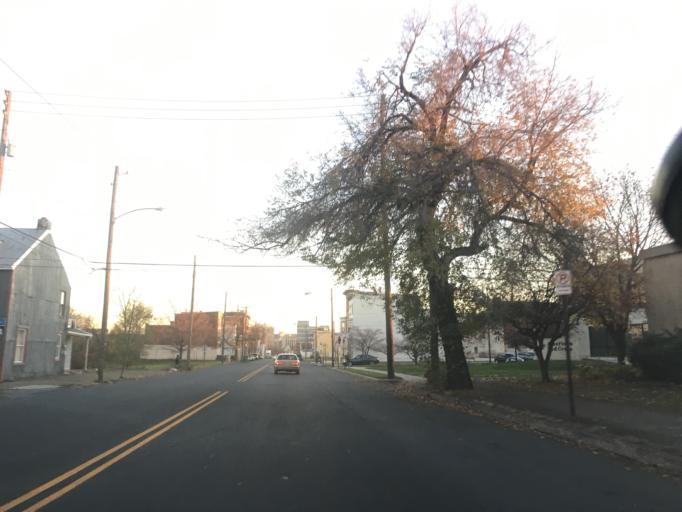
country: US
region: Pennsylvania
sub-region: Dauphin County
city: Harrisburg
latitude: 40.2780
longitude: -76.8892
